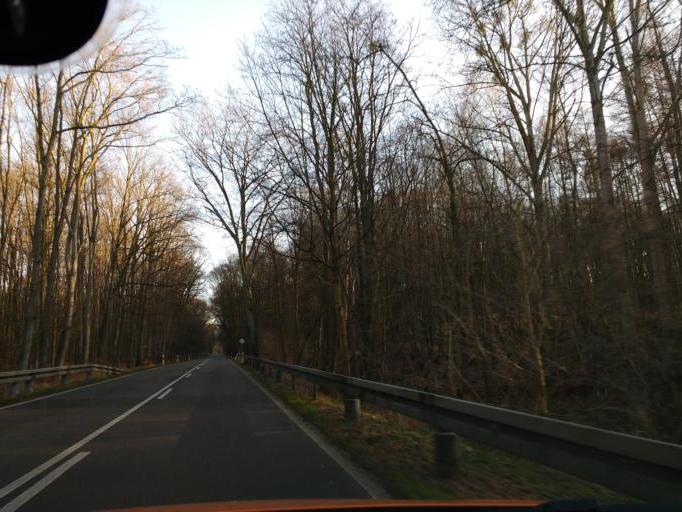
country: DE
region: Brandenburg
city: Werftpfuhl
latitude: 52.6611
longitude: 13.8497
